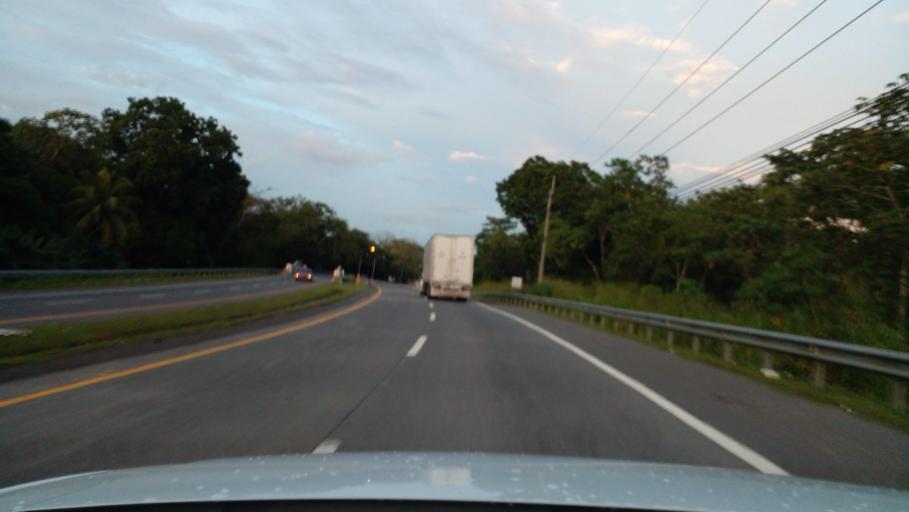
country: PA
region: Chiriqui
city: Tijera
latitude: 8.4716
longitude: -82.5429
